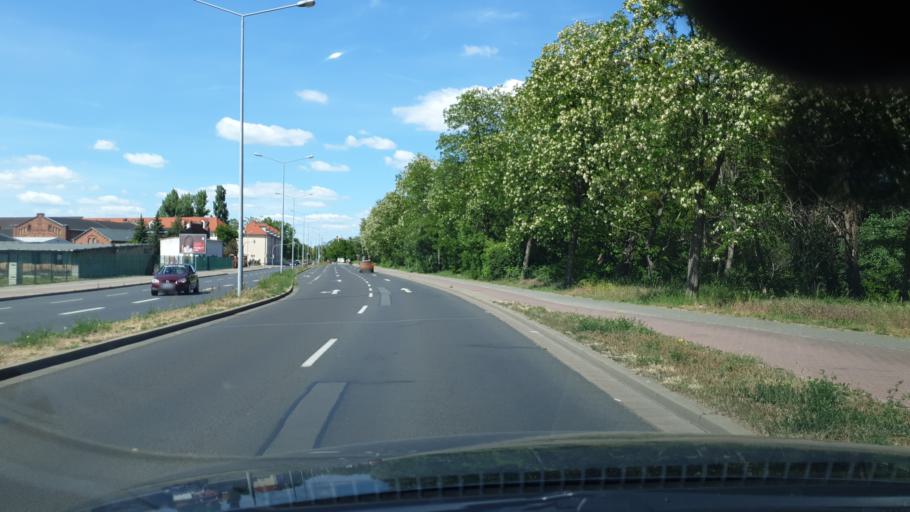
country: DE
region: Saxony-Anhalt
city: Dessau
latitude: 51.8156
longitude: 12.2502
